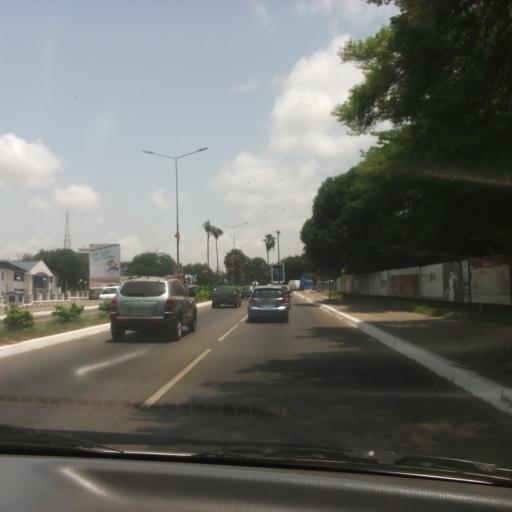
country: GH
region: Greater Accra
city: Accra
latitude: 5.5583
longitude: -0.1980
